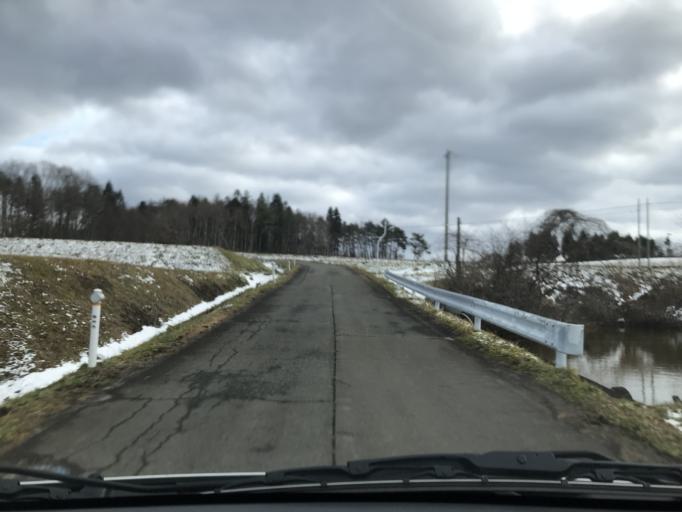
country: JP
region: Iwate
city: Ichinoseki
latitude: 38.9895
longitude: 141.0011
